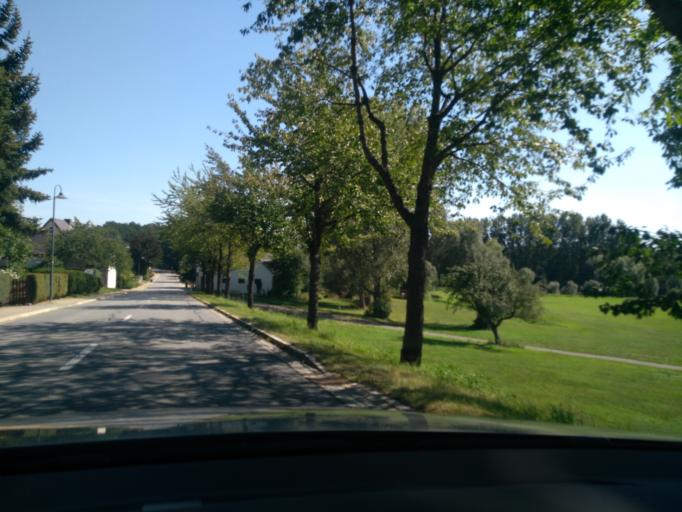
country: DE
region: Saxony
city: Goda
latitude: 51.2070
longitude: 14.3020
